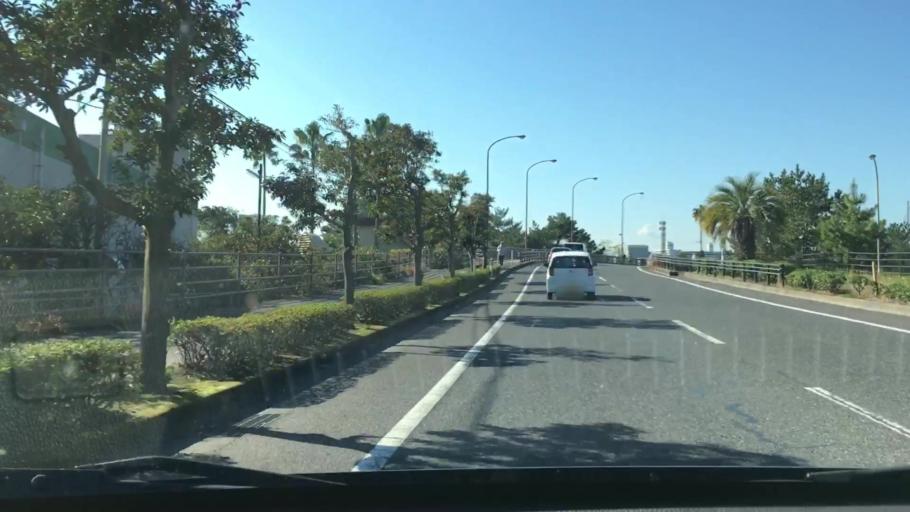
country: JP
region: Kagoshima
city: Kagoshima-shi
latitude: 31.6045
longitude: 130.5710
